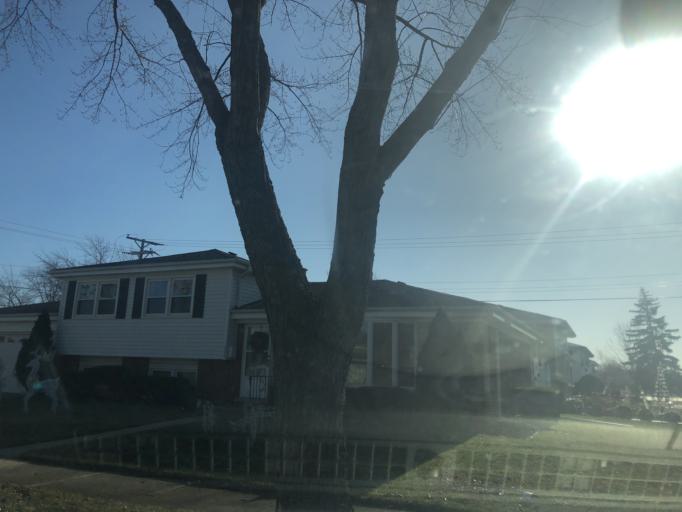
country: US
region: Illinois
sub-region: DuPage County
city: Addison
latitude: 41.9259
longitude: -87.9981
